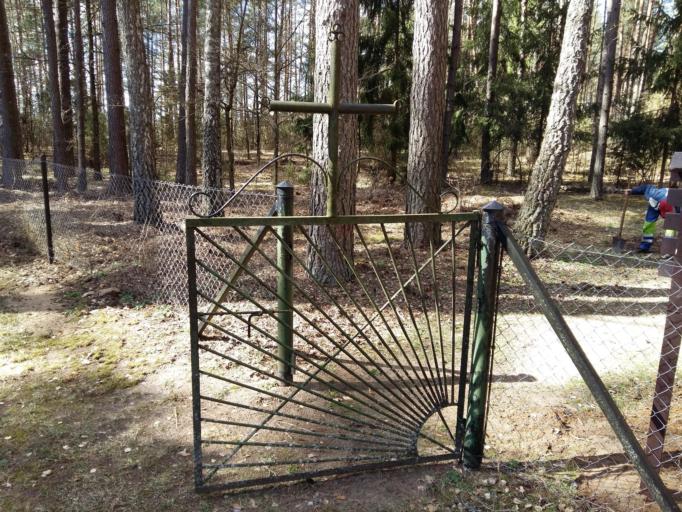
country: LT
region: Alytaus apskritis
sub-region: Alytaus rajonas
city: Daugai
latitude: 54.1163
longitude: 24.2620
